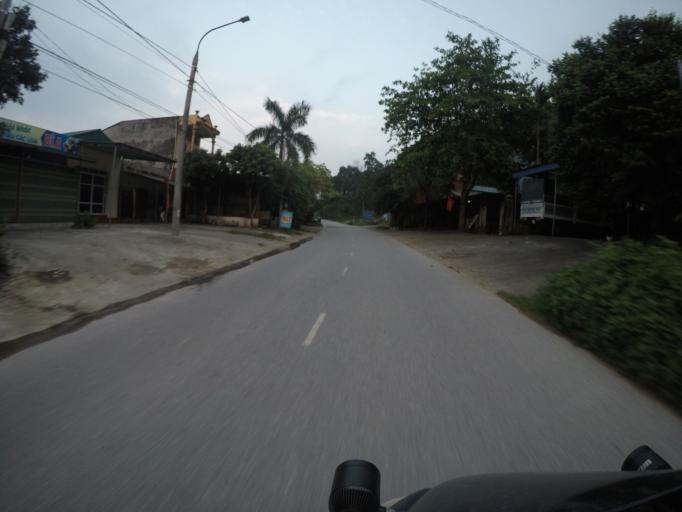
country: VN
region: Thai Nguyen
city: Chua Hang
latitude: 21.5871
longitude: 105.7334
